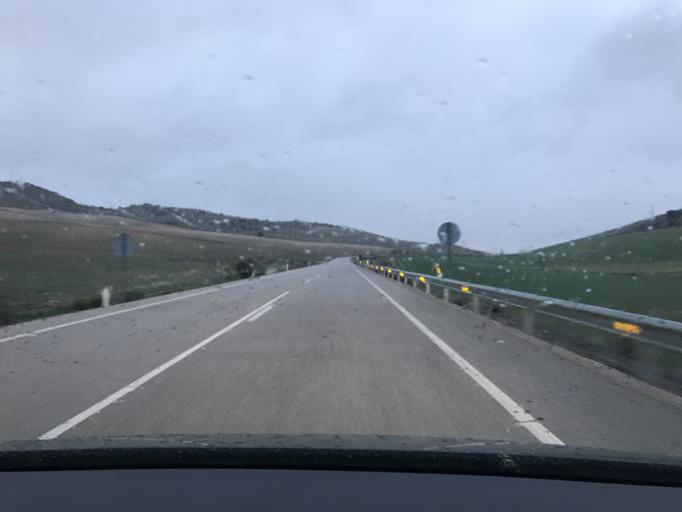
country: ES
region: Andalusia
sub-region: Provincia de Granada
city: Campotejar
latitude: 37.4659
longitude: -3.5923
